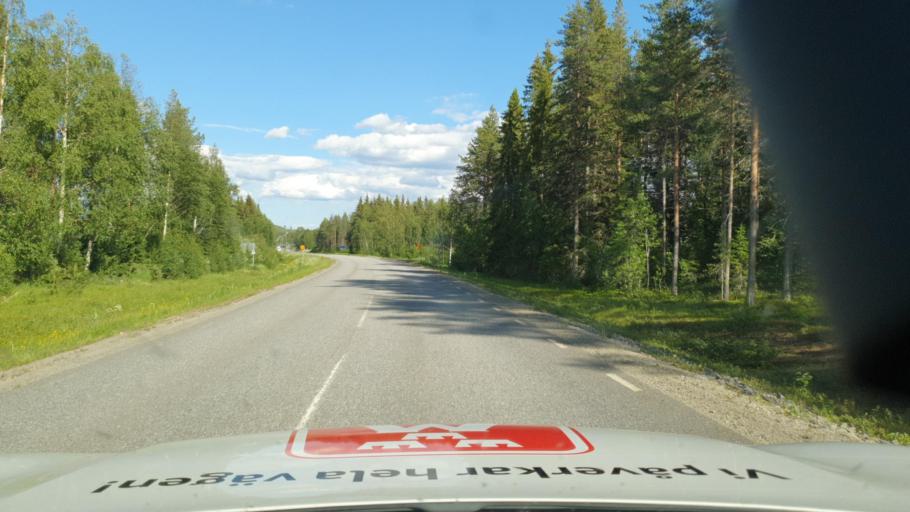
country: SE
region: Vaesterbotten
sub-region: Skelleftea Kommun
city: Langsele
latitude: 64.7937
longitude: 20.0249
